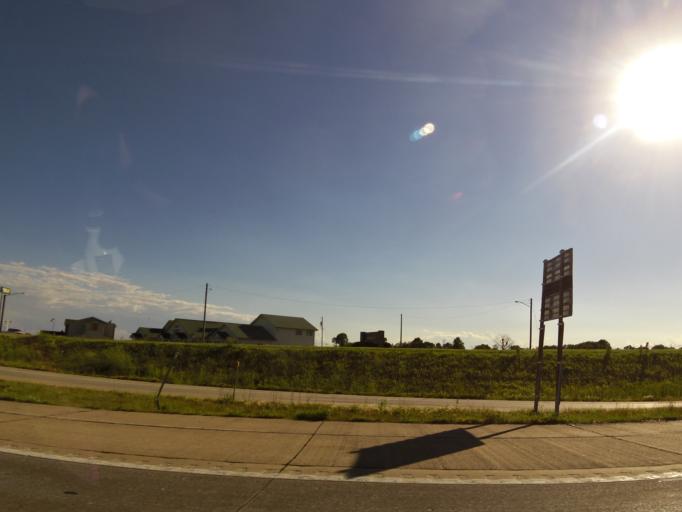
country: US
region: Missouri
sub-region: Pike County
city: Bowling Green
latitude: 39.3360
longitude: -91.1802
